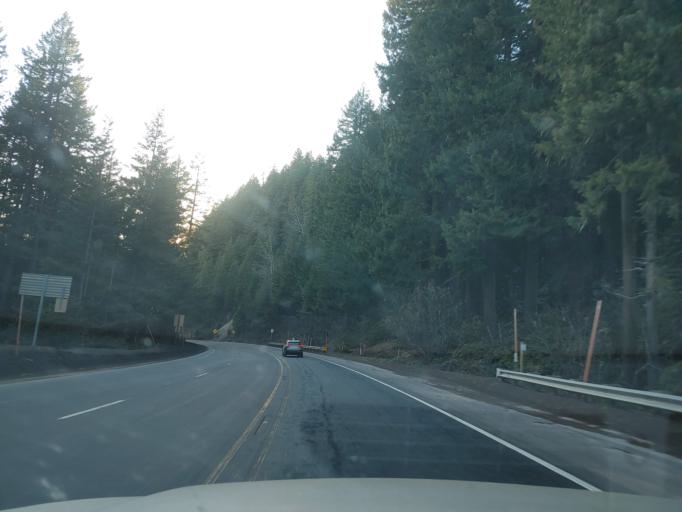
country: US
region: Oregon
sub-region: Lane County
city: Oakridge
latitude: 43.6136
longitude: -122.1275
